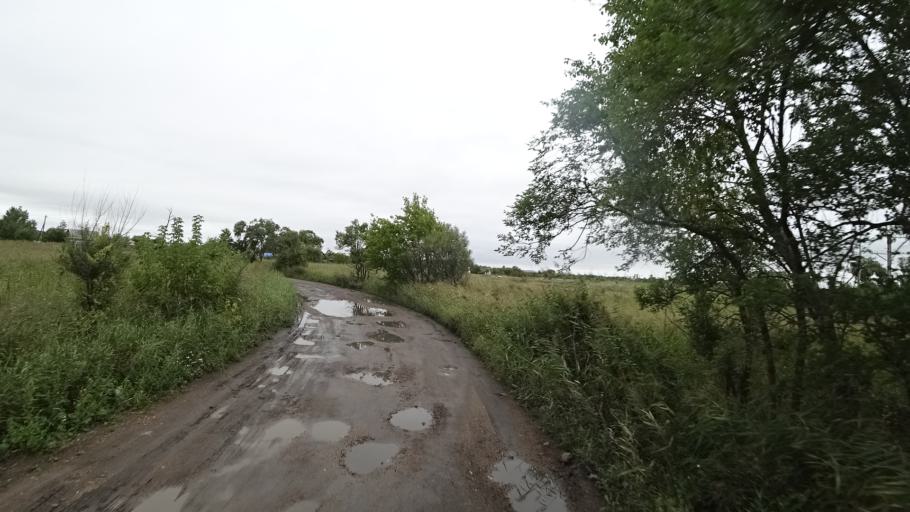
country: RU
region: Primorskiy
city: Chernigovka
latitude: 44.3423
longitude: 132.5361
